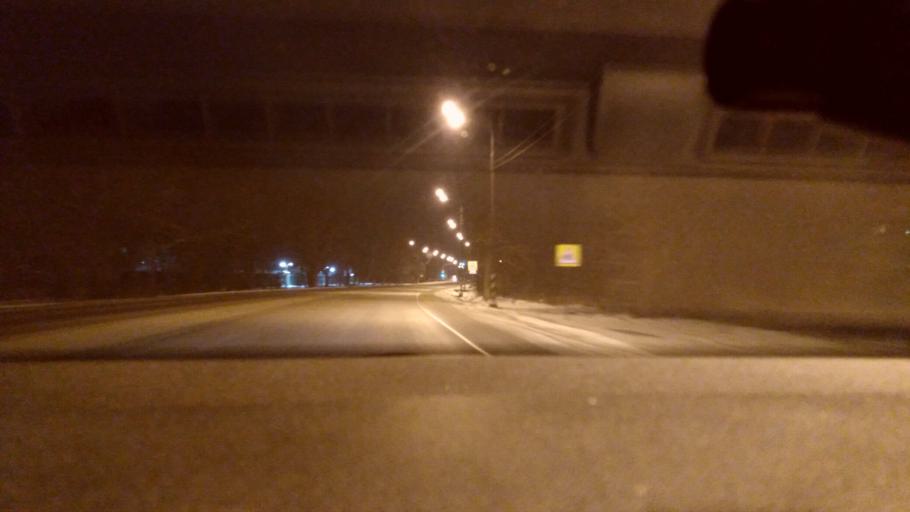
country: RU
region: Moskovskaya
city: Troitskoye
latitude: 55.2094
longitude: 38.6065
